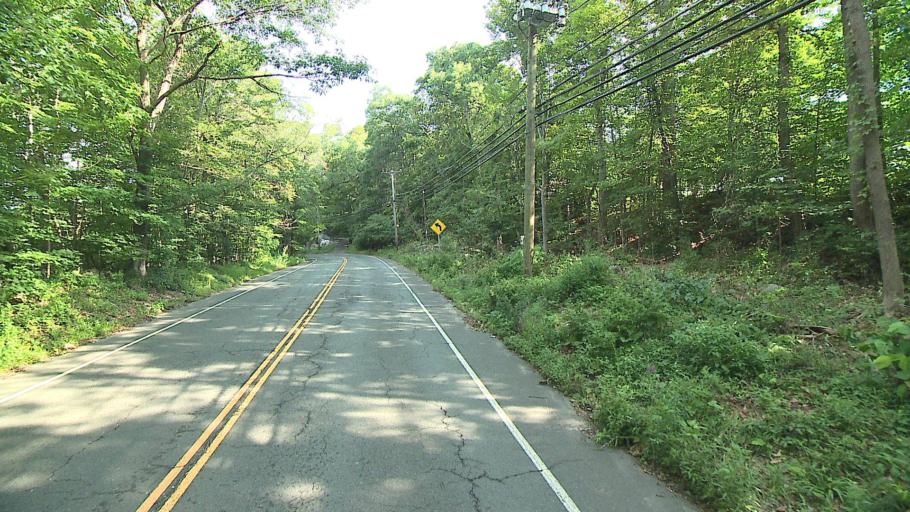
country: US
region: Connecticut
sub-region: Fairfield County
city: Danbury
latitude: 41.4214
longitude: -73.4689
